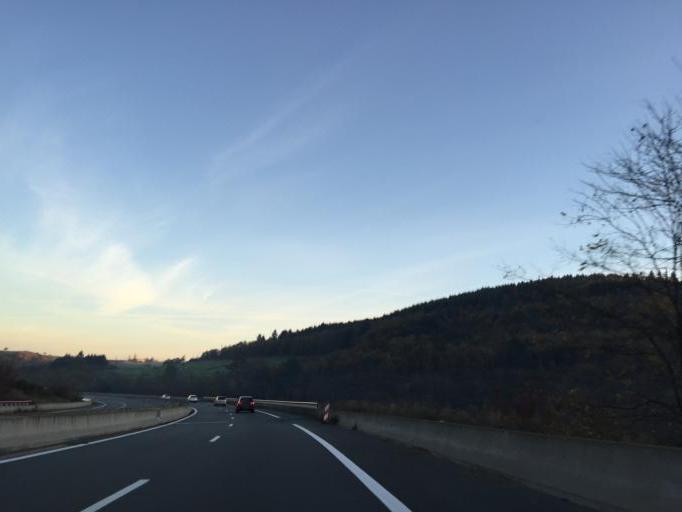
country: FR
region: Rhone-Alpes
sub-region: Departement de la Loire
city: Commelle-Vernay
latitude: 45.9648
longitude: 4.1345
